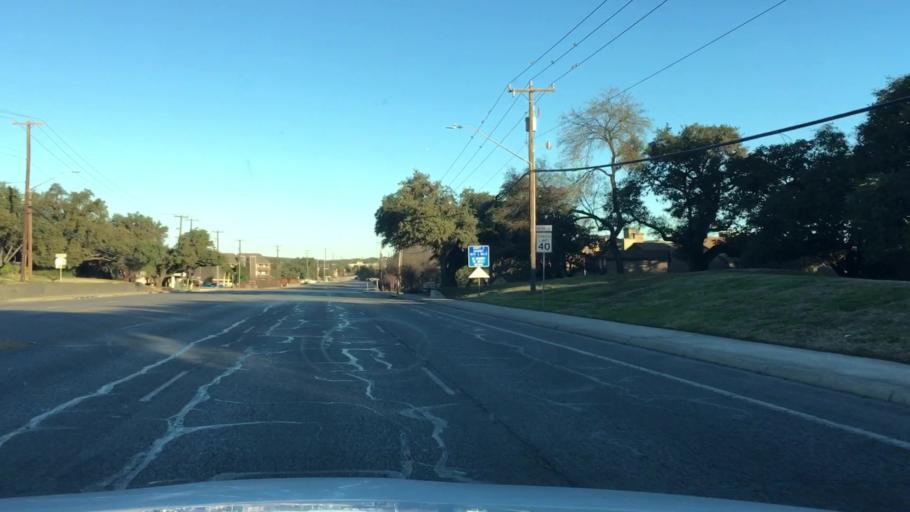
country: US
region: Texas
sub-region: Bexar County
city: Castle Hills
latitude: 29.5523
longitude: -98.5131
